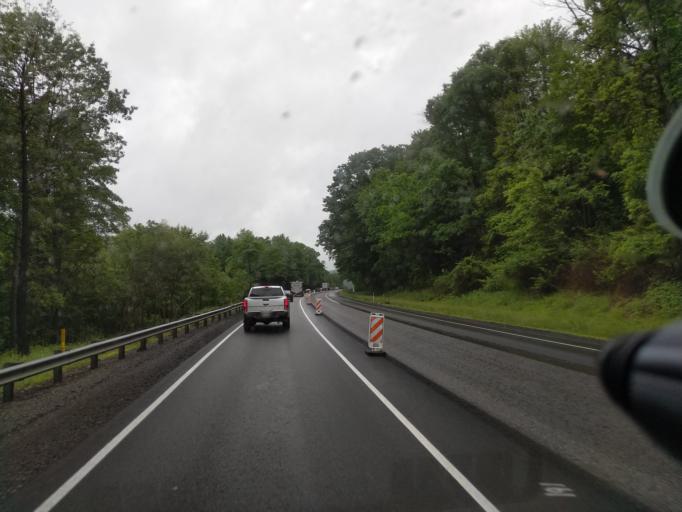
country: US
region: Pennsylvania
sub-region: Jefferson County
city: Brookville
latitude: 41.1496
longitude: -78.9949
